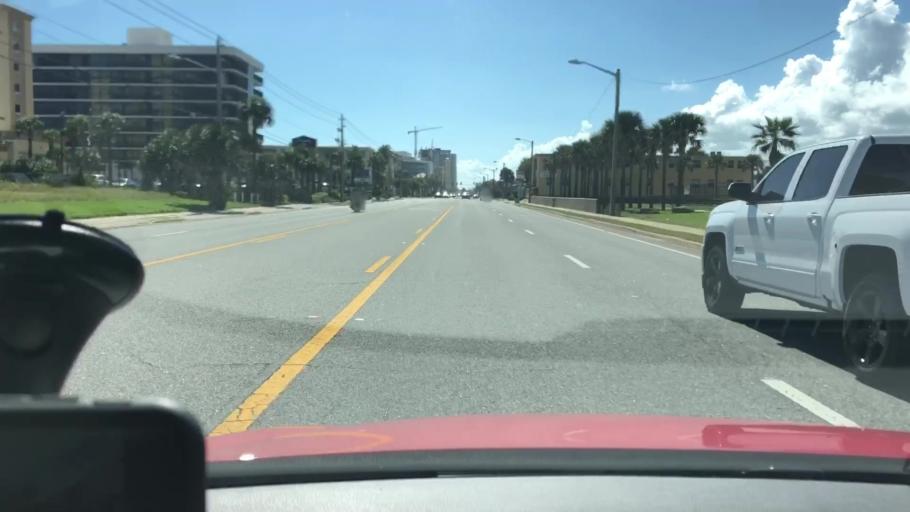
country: US
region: Florida
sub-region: Volusia County
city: Holly Hill
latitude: 29.2452
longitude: -81.0171
